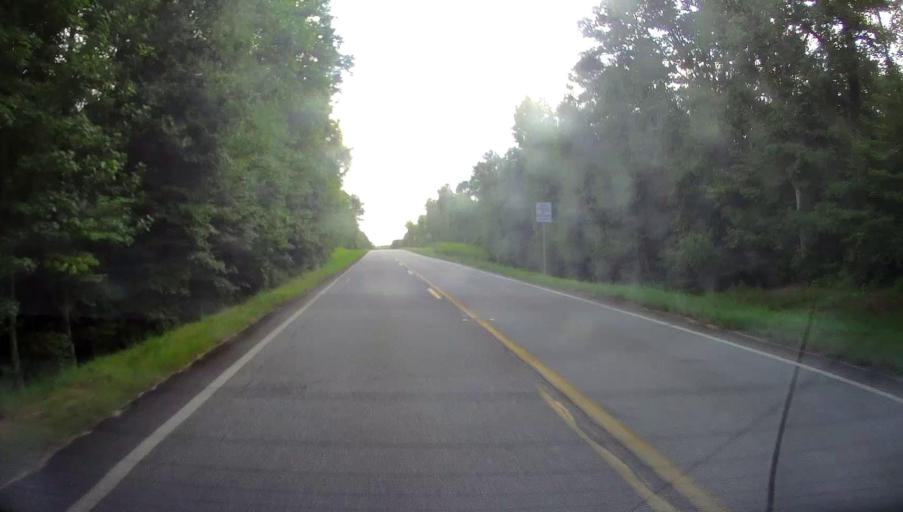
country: US
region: Georgia
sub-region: Crawford County
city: Knoxville
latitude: 32.8481
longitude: -84.0074
